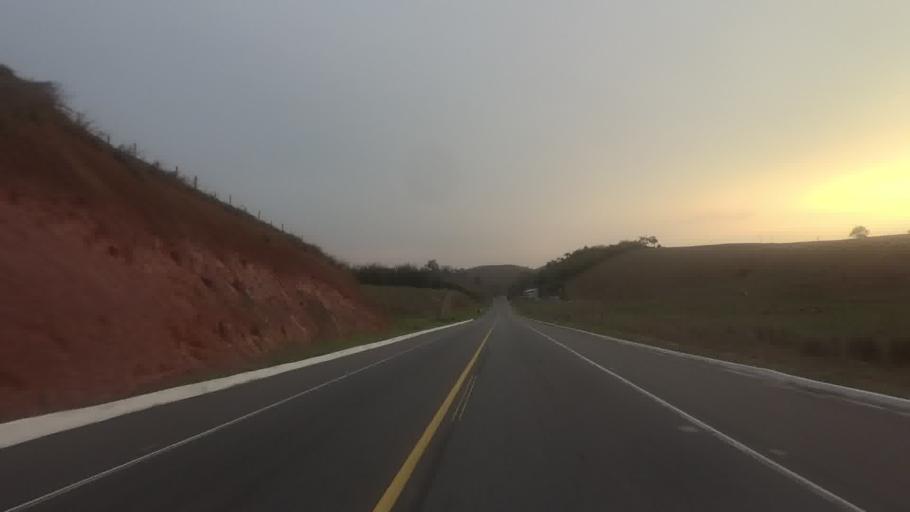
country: BR
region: Minas Gerais
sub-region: Recreio
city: Recreio
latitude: -21.7501
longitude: -42.4748
